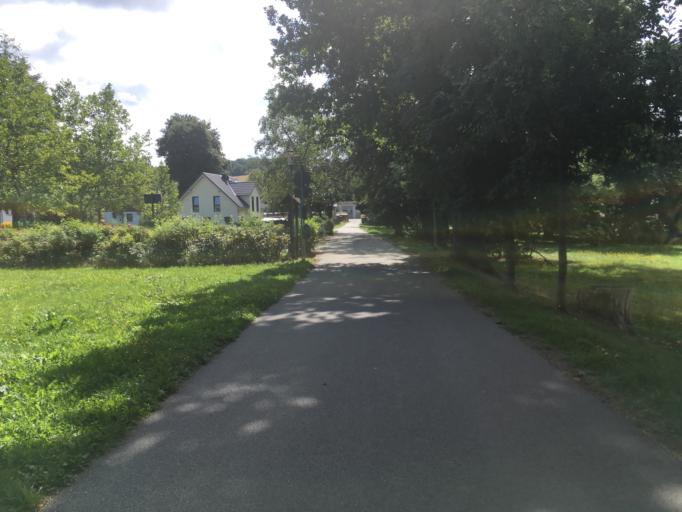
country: DE
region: Saxony
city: Waldenburg
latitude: 50.8678
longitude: 12.6113
